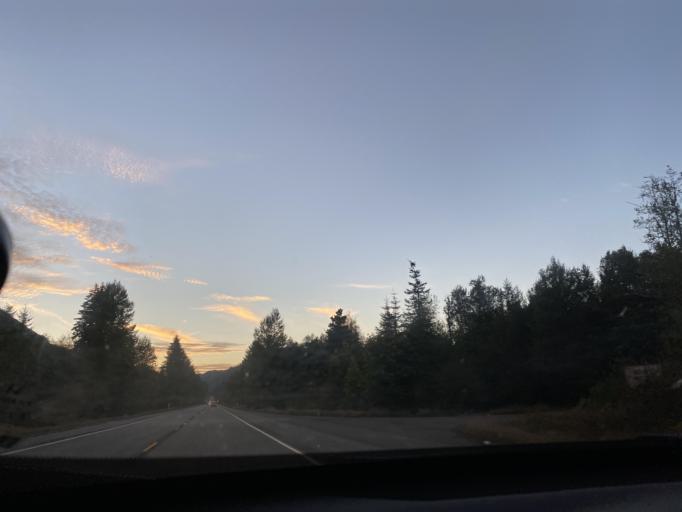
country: US
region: Washington
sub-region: Clallam County
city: Port Angeles
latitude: 48.0657
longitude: -123.6086
